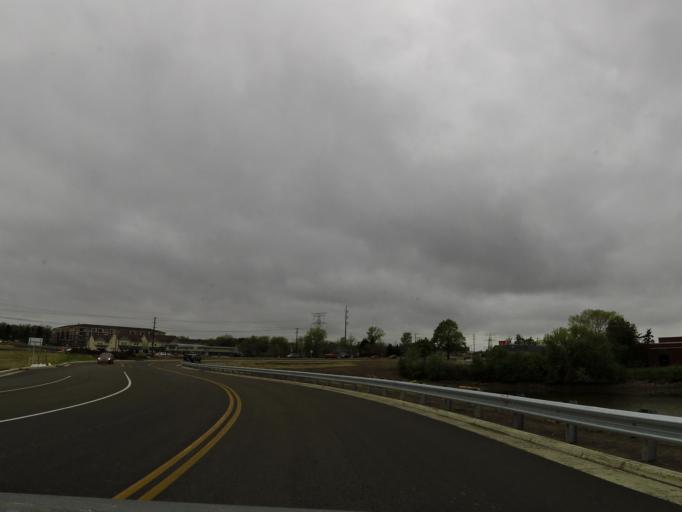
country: US
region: Minnesota
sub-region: Washington County
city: Stillwater
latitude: 45.0374
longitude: -92.8220
